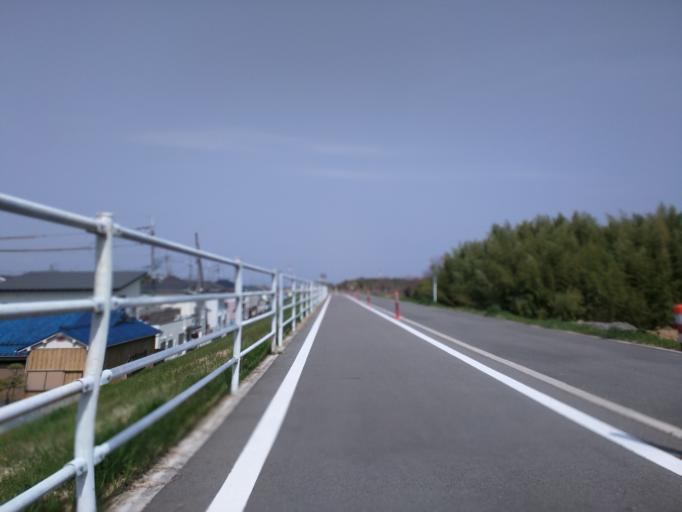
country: JP
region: Kyoto
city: Tanabe
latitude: 34.7840
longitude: 135.7999
